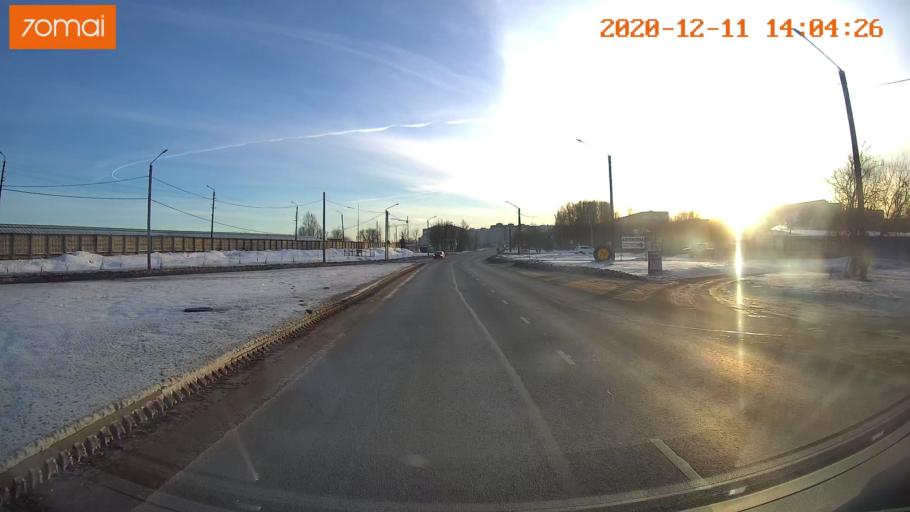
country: RU
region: Kostroma
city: Oktyabr'skiy
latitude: 57.7555
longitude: 41.0162
